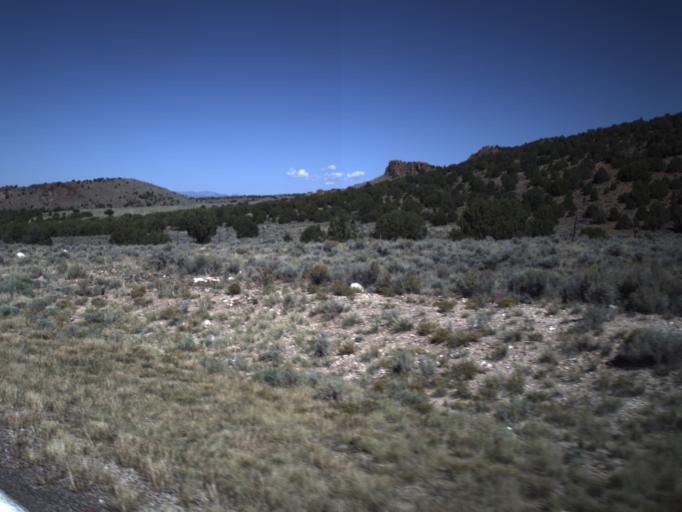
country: US
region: Utah
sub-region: Washington County
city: Enterprise
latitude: 37.6687
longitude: -113.4806
